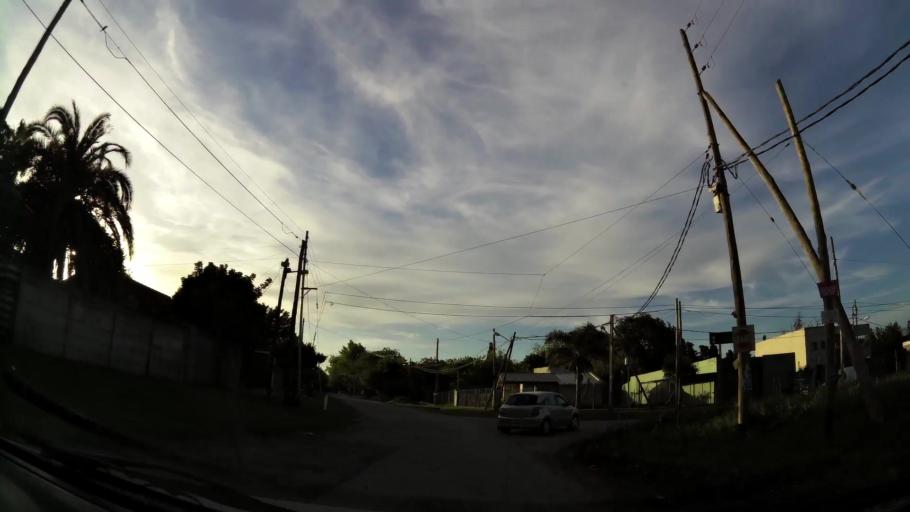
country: AR
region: Buenos Aires
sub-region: Partido de Quilmes
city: Quilmes
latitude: -34.7902
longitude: -58.1917
